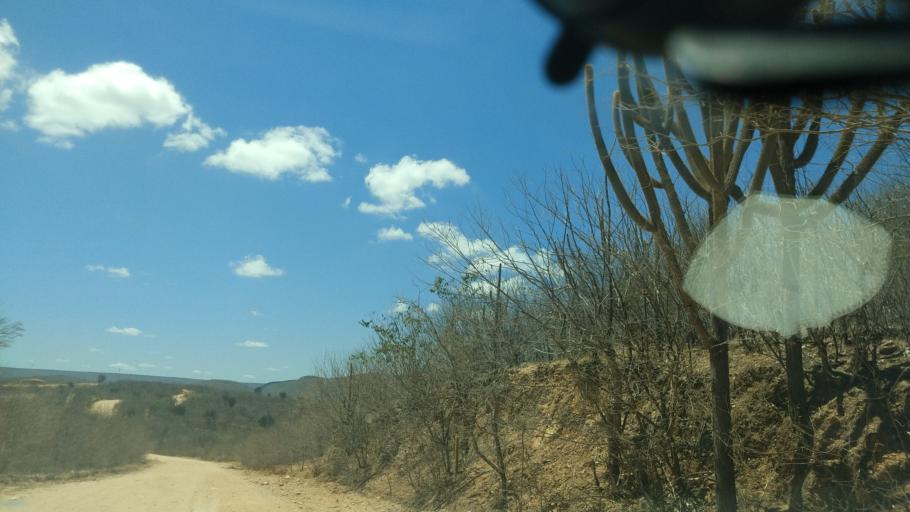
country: BR
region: Rio Grande do Norte
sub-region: Cerro Cora
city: Cerro Cora
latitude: -6.0111
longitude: -36.3013
